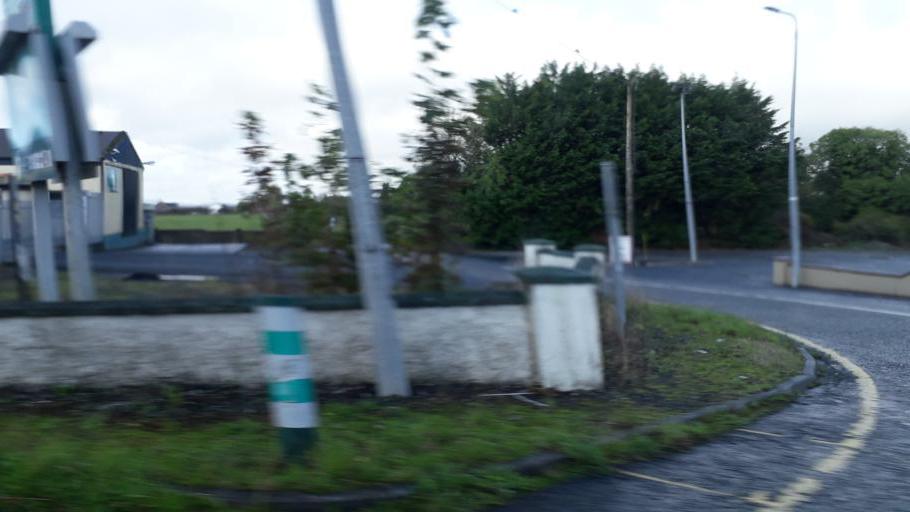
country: IE
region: Connaught
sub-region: Roscommon
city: Castlerea
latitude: 53.8819
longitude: -8.4499
